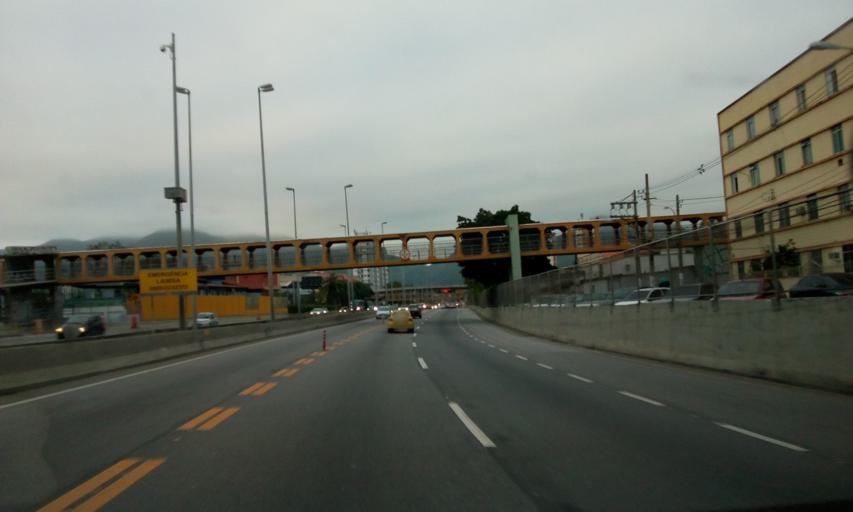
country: BR
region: Rio de Janeiro
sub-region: Rio De Janeiro
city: Rio de Janeiro
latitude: -22.8869
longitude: -43.2928
